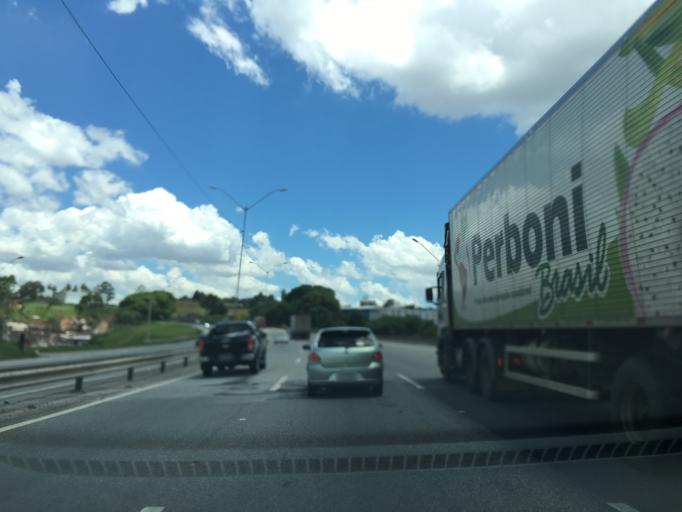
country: BR
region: Sao Paulo
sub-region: Guarulhos
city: Guarulhos
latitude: -23.4113
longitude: -46.5817
